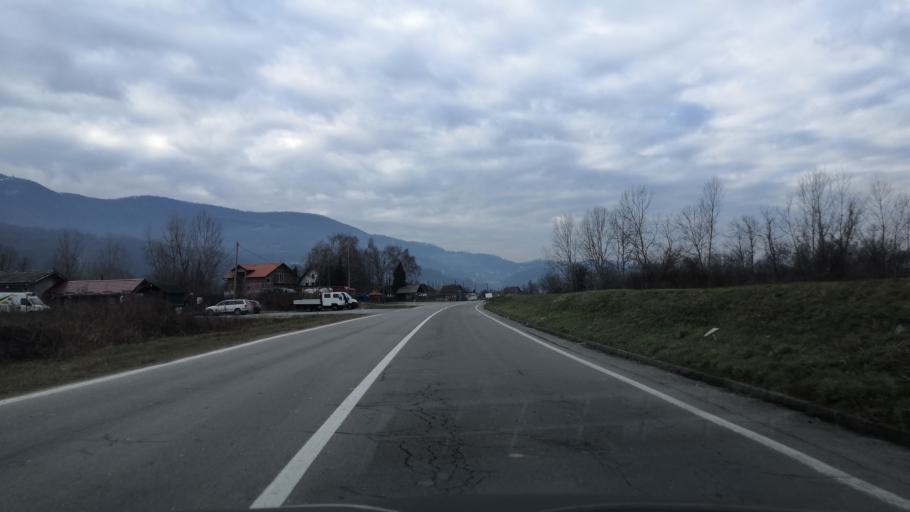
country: RS
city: Trsic
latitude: 44.5260
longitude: 19.1771
